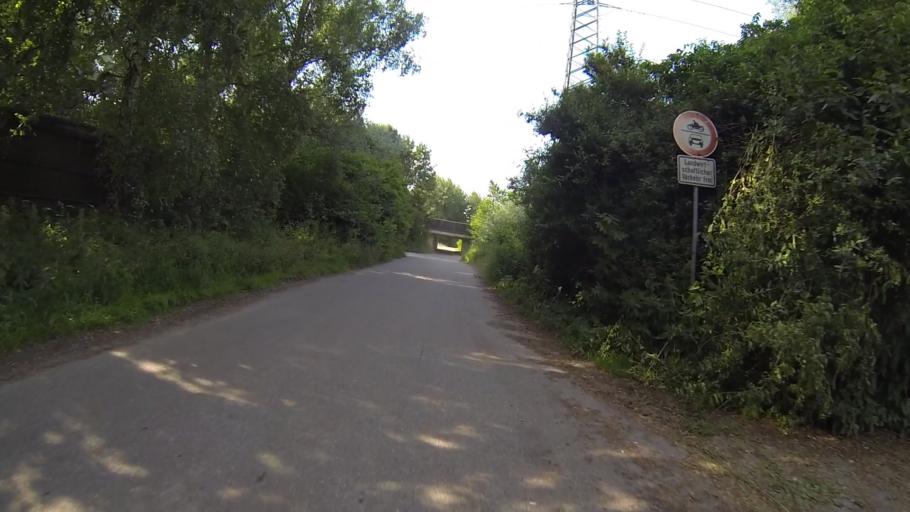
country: DE
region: Bavaria
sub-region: Swabia
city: Neu-Ulm
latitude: 48.3884
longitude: 10.0466
